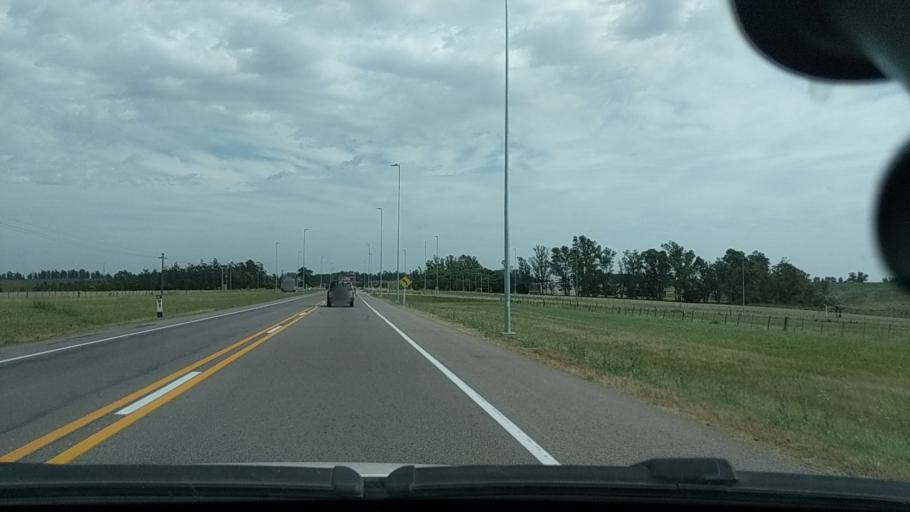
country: UY
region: Florida
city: Florida
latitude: -34.1361
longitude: -56.1833
